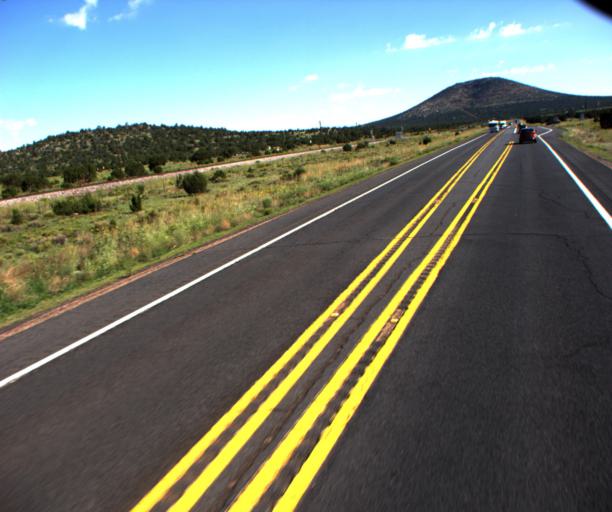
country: US
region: Arizona
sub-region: Coconino County
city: Williams
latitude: 35.3654
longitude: -112.1656
